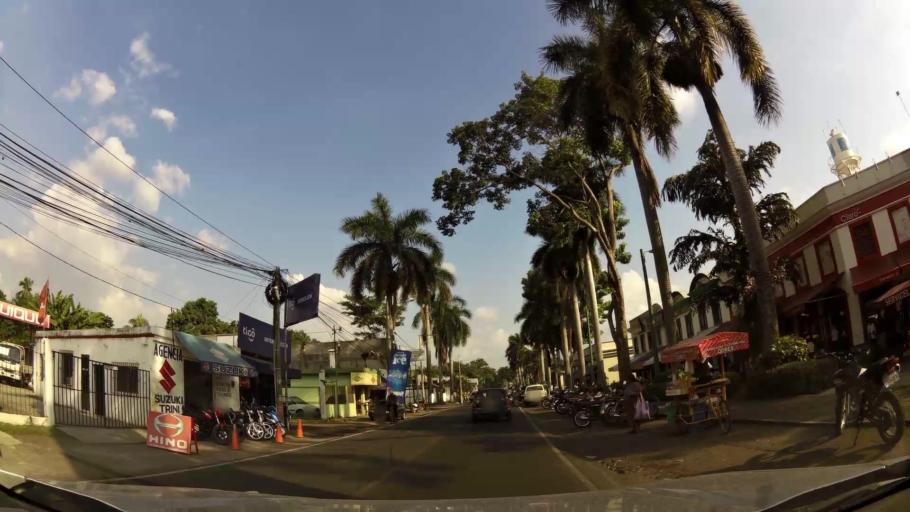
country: GT
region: Retalhuleu
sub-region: Municipio de Retalhuleu
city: Retalhuleu
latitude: 14.5330
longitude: -91.6803
